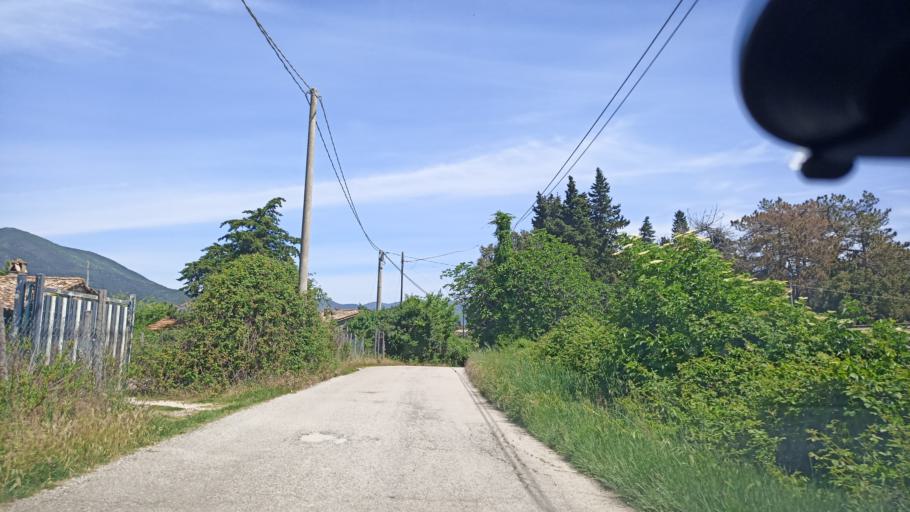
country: IT
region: Latium
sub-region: Provincia di Rieti
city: Torri in Sabina
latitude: 42.3534
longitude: 12.6313
